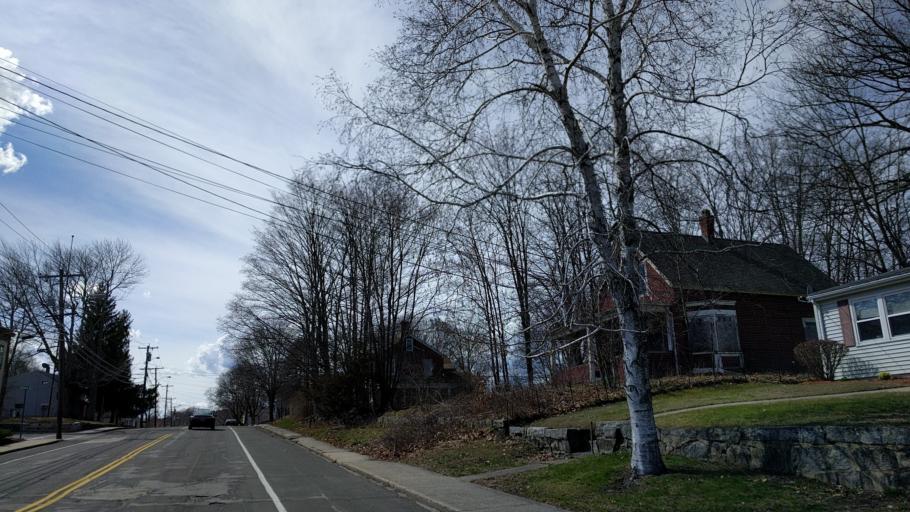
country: US
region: Massachusetts
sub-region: Worcester County
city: Uxbridge
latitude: 42.0927
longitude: -71.6375
